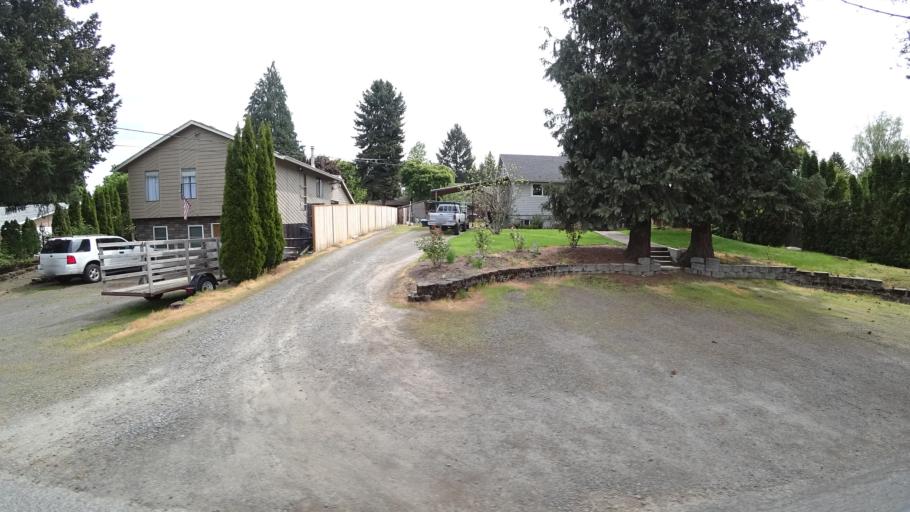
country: US
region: Oregon
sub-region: Washington County
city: Hillsboro
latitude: 45.5260
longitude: -123.0034
